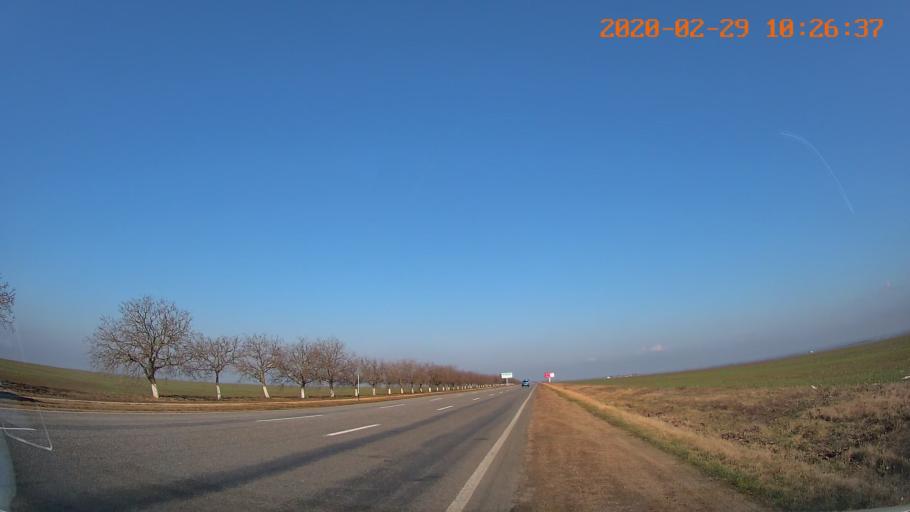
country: MD
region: Telenesti
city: Tiraspolul Nou
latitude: 46.8873
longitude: 29.6017
